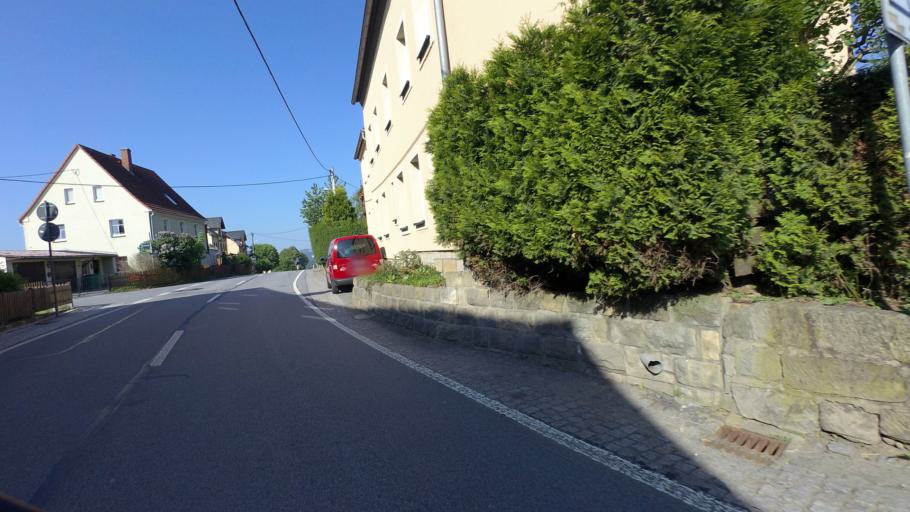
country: DE
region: Saxony
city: Bad Schandau
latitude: 50.9351
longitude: 14.1810
